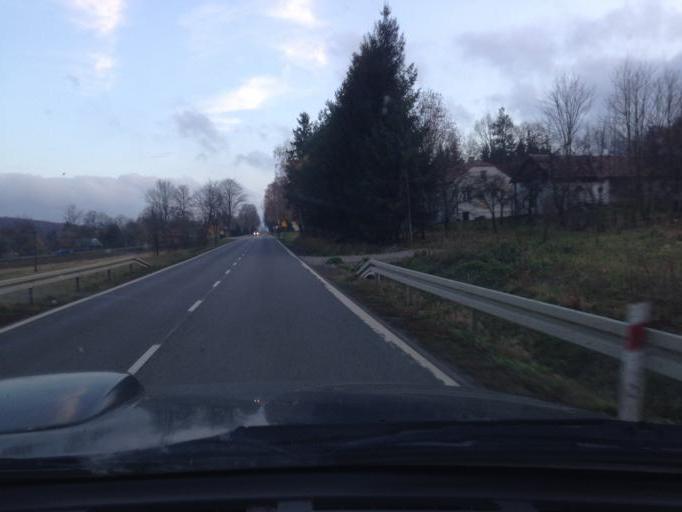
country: PL
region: Subcarpathian Voivodeship
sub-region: Powiat jasielski
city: Osiek Jasielski
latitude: 49.6437
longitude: 21.5160
